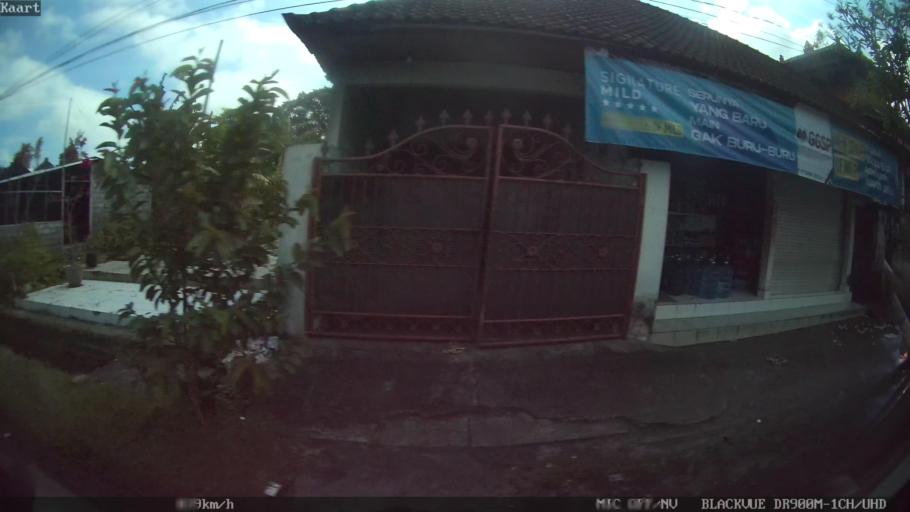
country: ID
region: Bali
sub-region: Kabupaten Gianyar
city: Ubud
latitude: -8.5280
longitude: 115.2995
